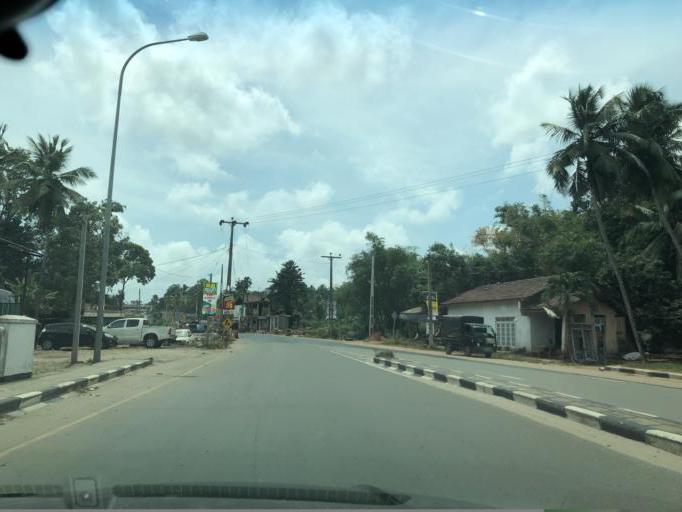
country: LK
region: Western
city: Homagama
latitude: 6.7842
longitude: 79.9798
